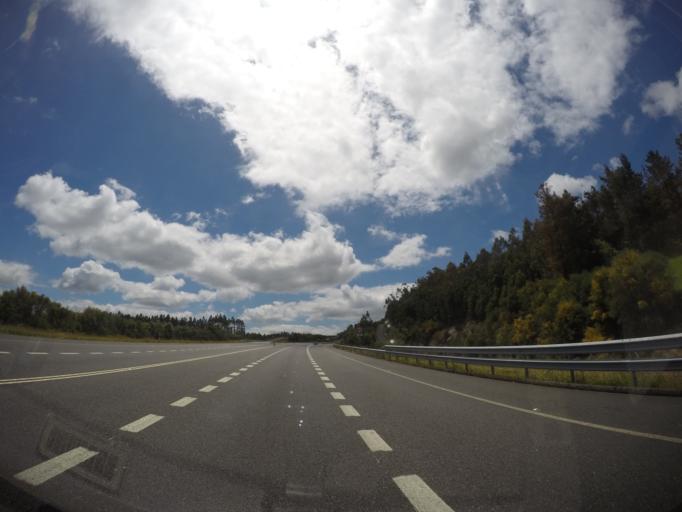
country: ES
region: Aragon
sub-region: Provincia de Zaragoza
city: Fuentes de Ebro
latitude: 41.4984
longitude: -0.6577
